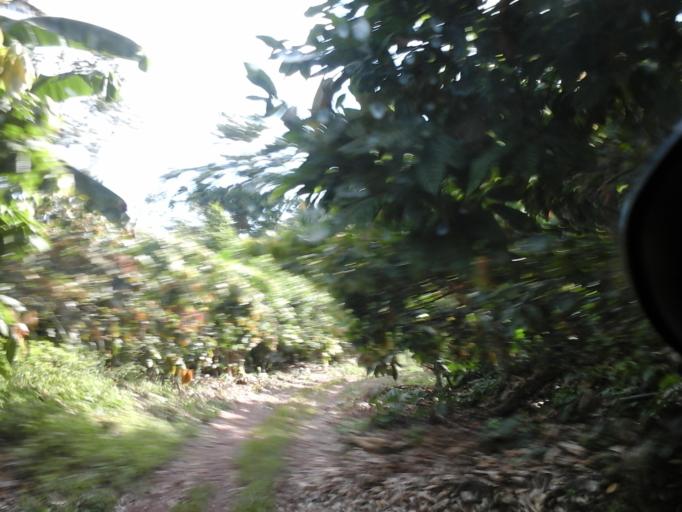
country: CO
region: Cesar
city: San Diego
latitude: 10.2883
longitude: -73.0838
